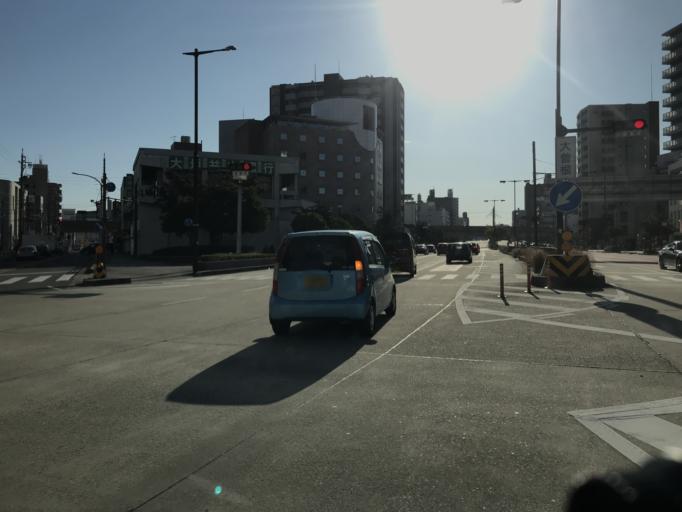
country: JP
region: Aichi
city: Nagoya-shi
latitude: 35.1901
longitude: 136.9302
